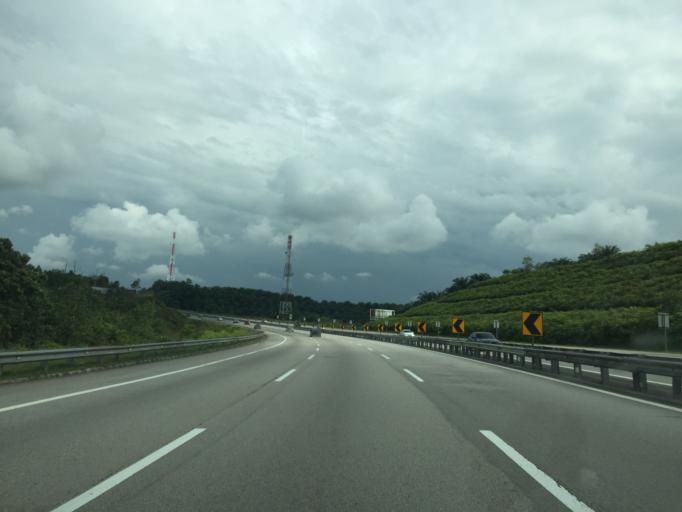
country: MY
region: Selangor
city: Batang Berjuntai
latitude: 3.6012
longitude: 101.5224
